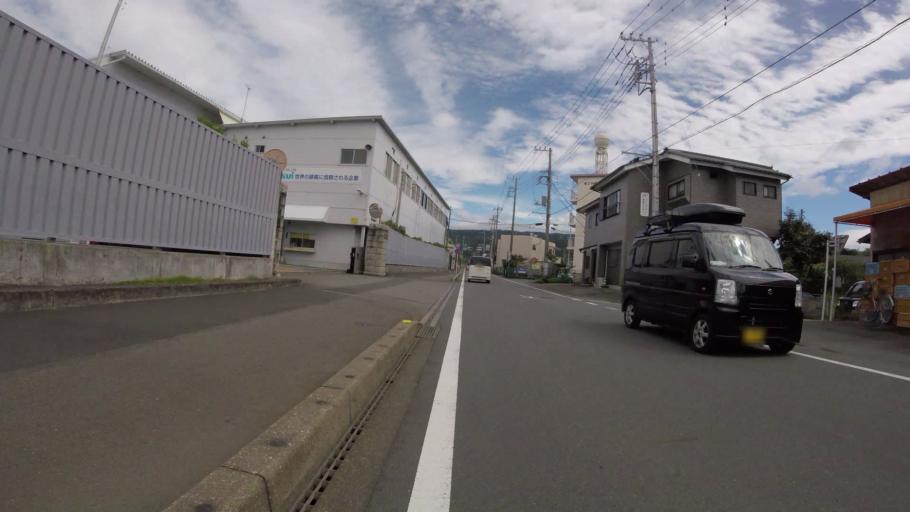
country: JP
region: Shizuoka
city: Mishima
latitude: 35.0546
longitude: 138.9460
